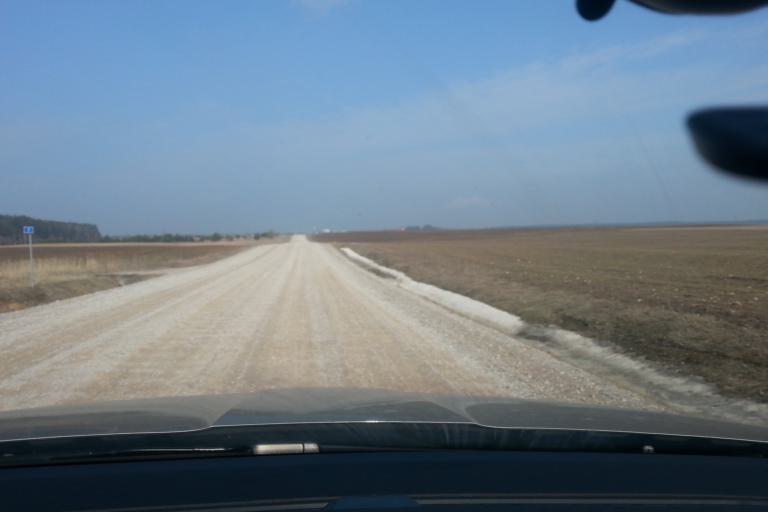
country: LT
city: Trakai
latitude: 54.5873
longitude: 24.9769
